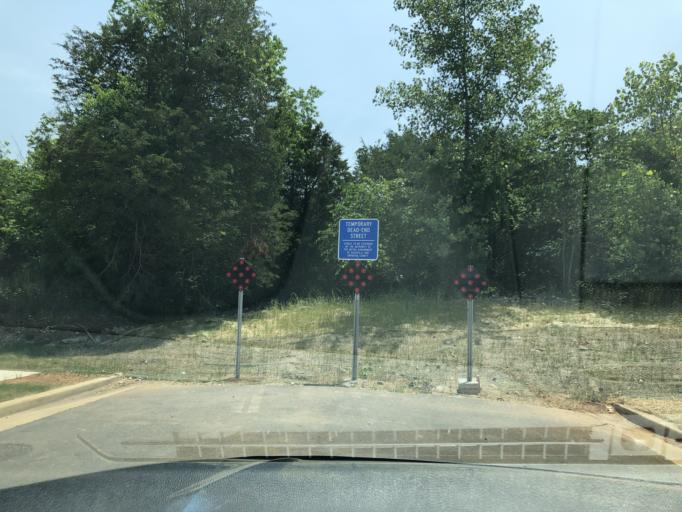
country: US
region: Tennessee
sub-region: Rutherford County
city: La Vergne
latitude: 36.0598
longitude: -86.6071
